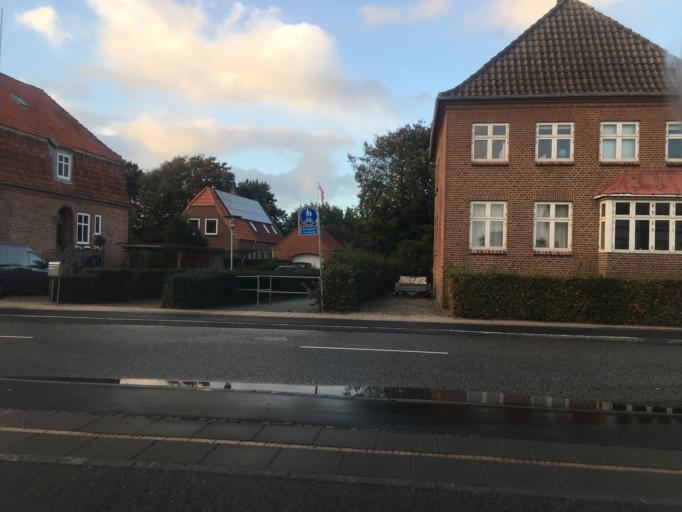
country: DK
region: South Denmark
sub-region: Tonder Kommune
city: Tonder
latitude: 54.9354
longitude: 8.8543
